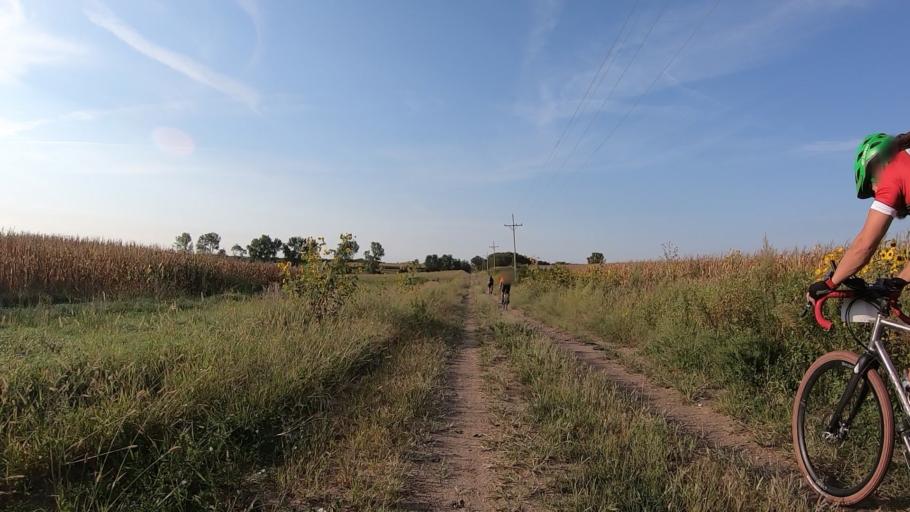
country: US
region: Kansas
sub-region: Marshall County
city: Blue Rapids
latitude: 39.7077
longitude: -96.7792
